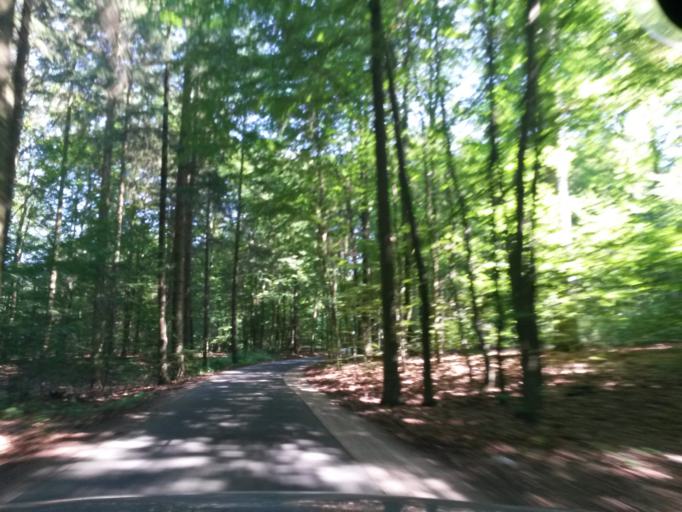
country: DE
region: Brandenburg
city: Marienwerder
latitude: 52.8993
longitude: 13.6702
